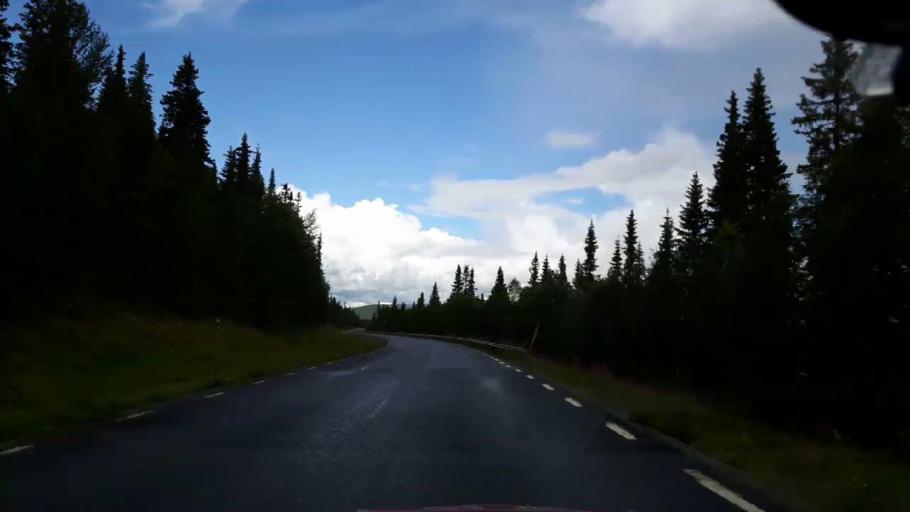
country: SE
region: Vaesterbotten
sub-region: Vilhelmina Kommun
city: Sjoberg
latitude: 65.0004
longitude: 15.1983
